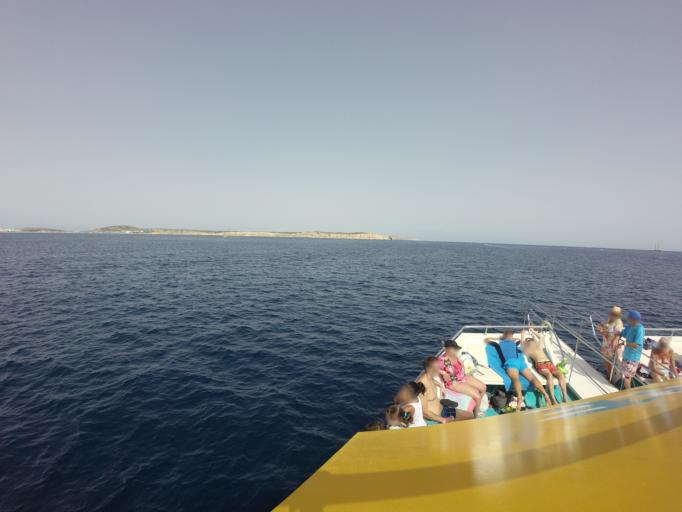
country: MT
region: Il-Mellieha
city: Mellieha
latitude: 35.9770
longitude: 14.3906
